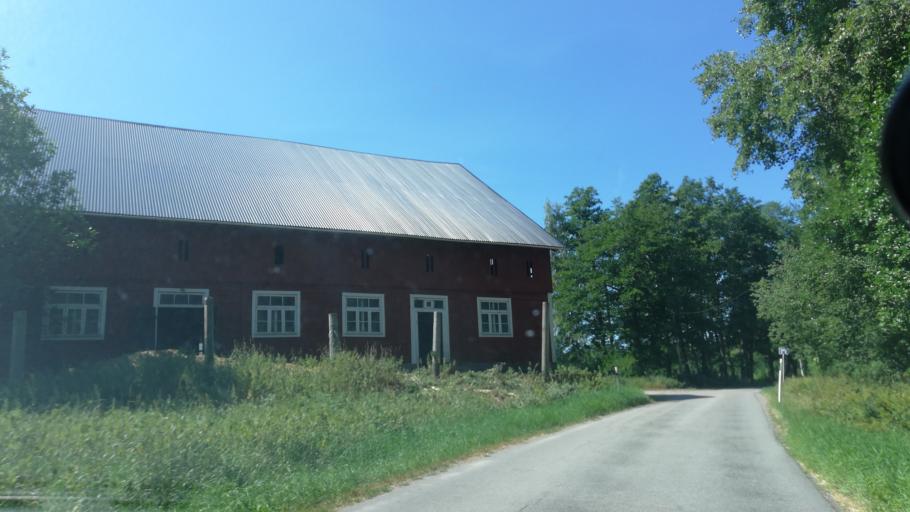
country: SE
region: OEstergoetland
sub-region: Finspangs Kommun
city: Finspang
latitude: 58.7331
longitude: 15.7208
